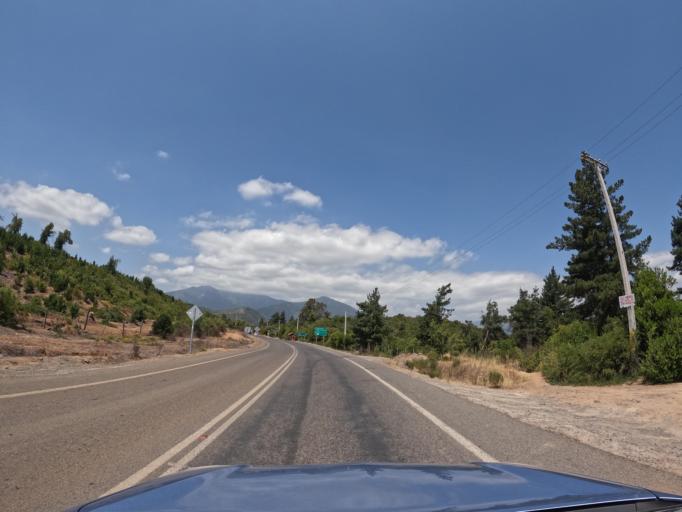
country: CL
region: Maule
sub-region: Provincia de Curico
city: Molina
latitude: -35.1818
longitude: -71.1127
